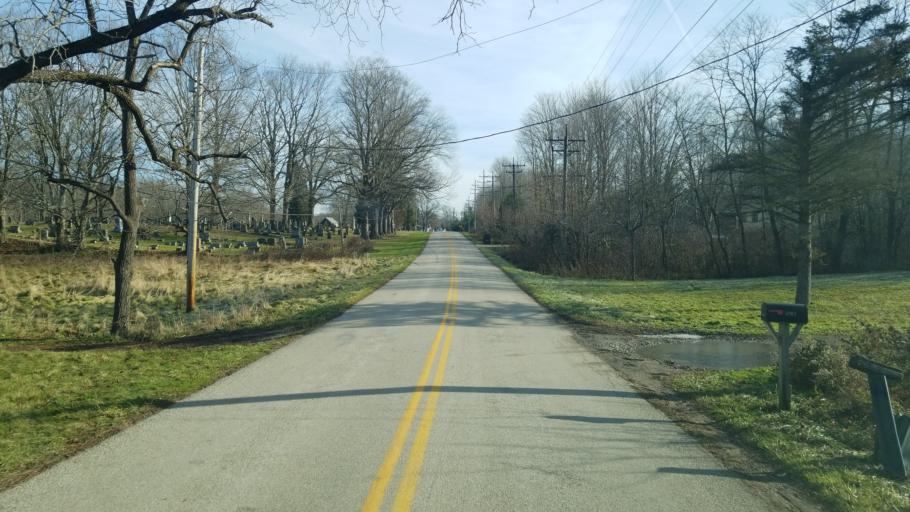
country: US
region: Ohio
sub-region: Ashtabula County
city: North Kingsville
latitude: 41.8446
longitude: -80.6703
